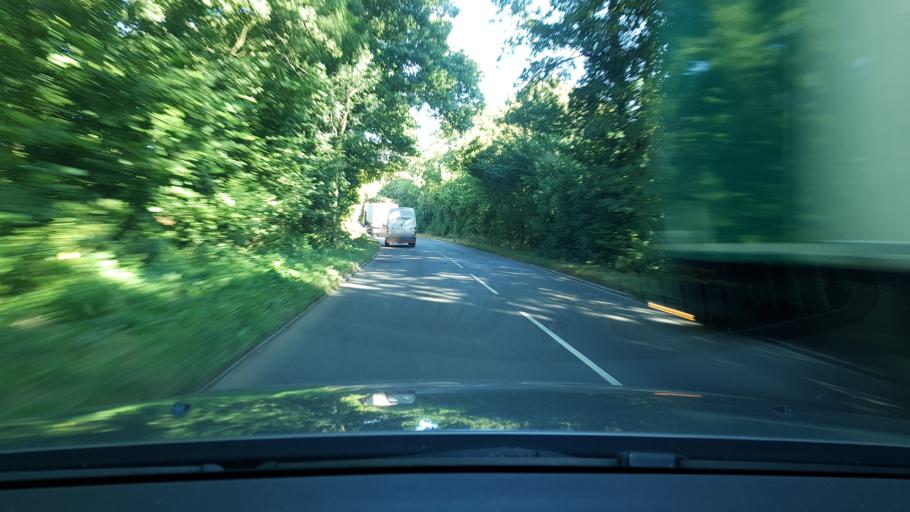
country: GB
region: England
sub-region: West Berkshire
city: Hungerford
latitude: 51.4616
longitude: -1.4854
